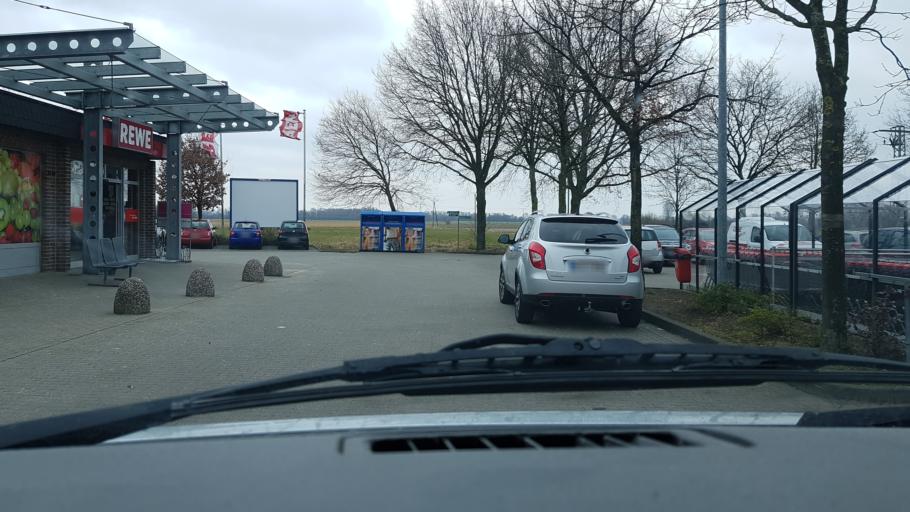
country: DE
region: North Rhine-Westphalia
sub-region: Regierungsbezirk Dusseldorf
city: Kranenburg
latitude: 51.7888
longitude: 6.0130
